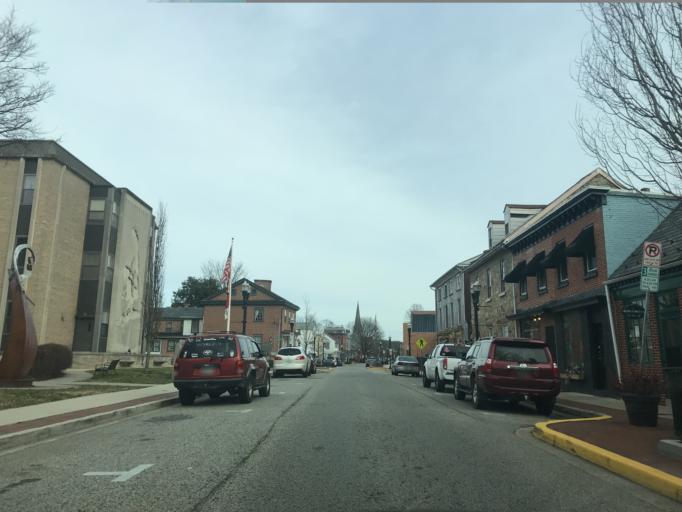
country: US
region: Maryland
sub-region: Cecil County
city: Elkton
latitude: 39.6082
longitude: -75.8290
